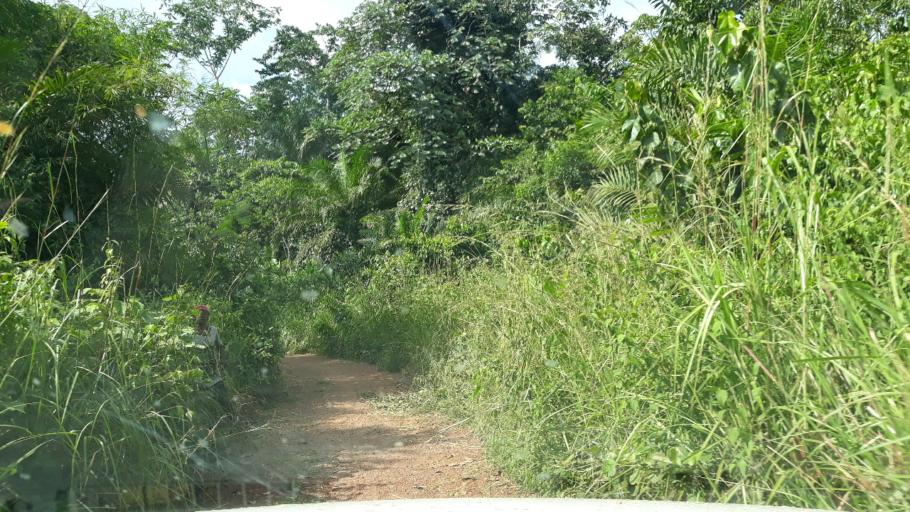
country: CD
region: Maniema
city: Kampene
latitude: -2.7569
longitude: 26.9279
